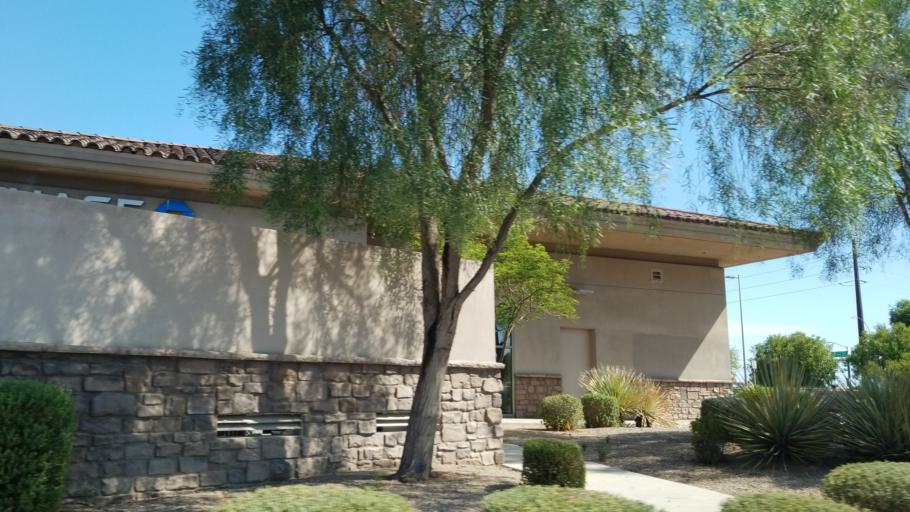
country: US
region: Arizona
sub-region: Maricopa County
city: Tolleson
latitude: 33.4221
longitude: -112.2218
